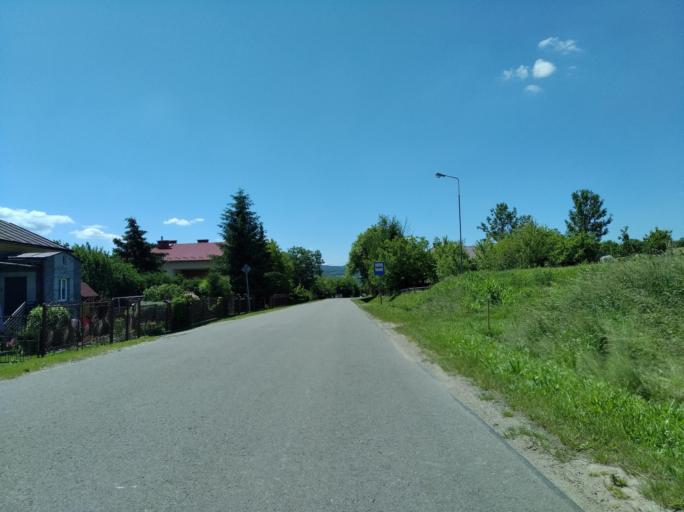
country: PL
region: Subcarpathian Voivodeship
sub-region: Powiat jasielski
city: Nowy Zmigrod
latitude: 49.6241
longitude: 21.5849
